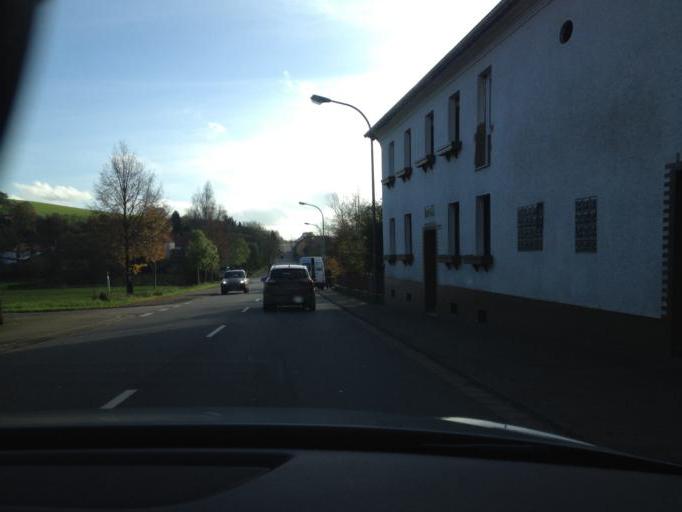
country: DE
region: Rheinland-Pfalz
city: Breitenbach
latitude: 49.4500
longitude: 7.2311
